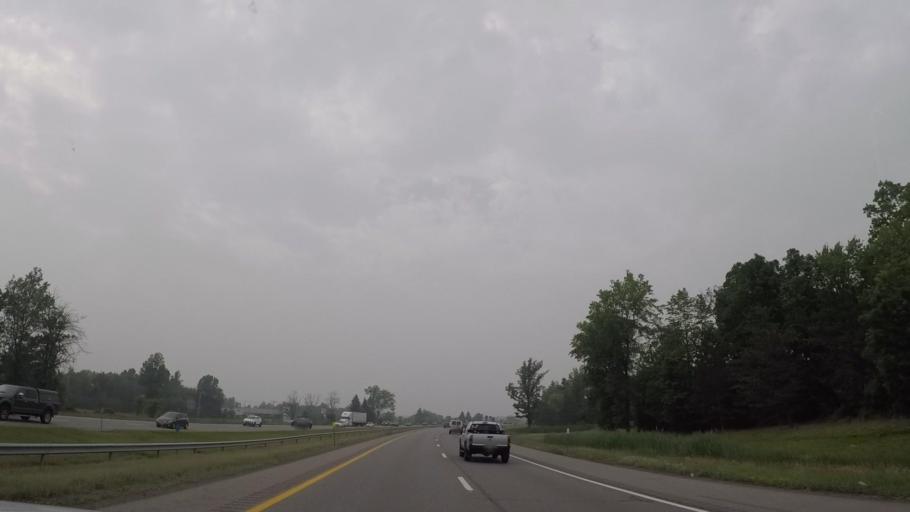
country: US
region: New York
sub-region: Erie County
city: Grandyle Village
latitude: 43.0137
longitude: -78.9680
